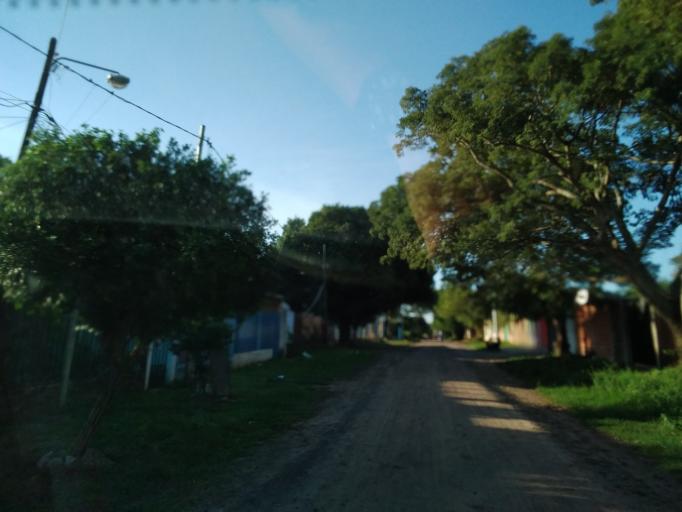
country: AR
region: Corrientes
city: Corrientes
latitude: -27.5036
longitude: -58.8062
